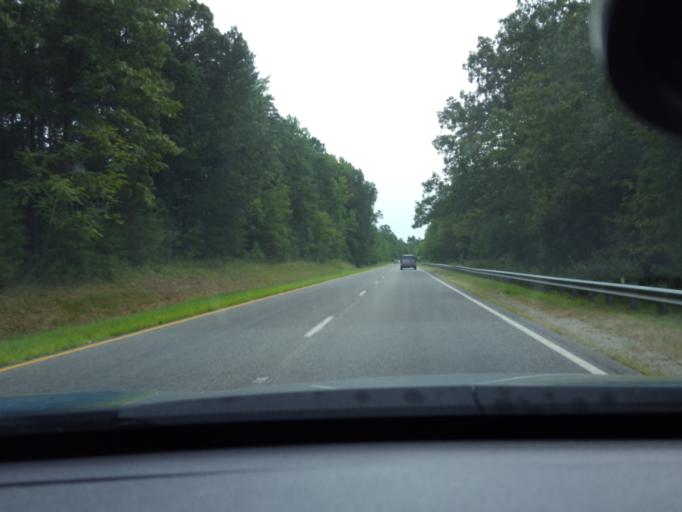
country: US
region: Virginia
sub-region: Caroline County
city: Bowling Green
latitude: 38.1070
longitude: -77.2674
